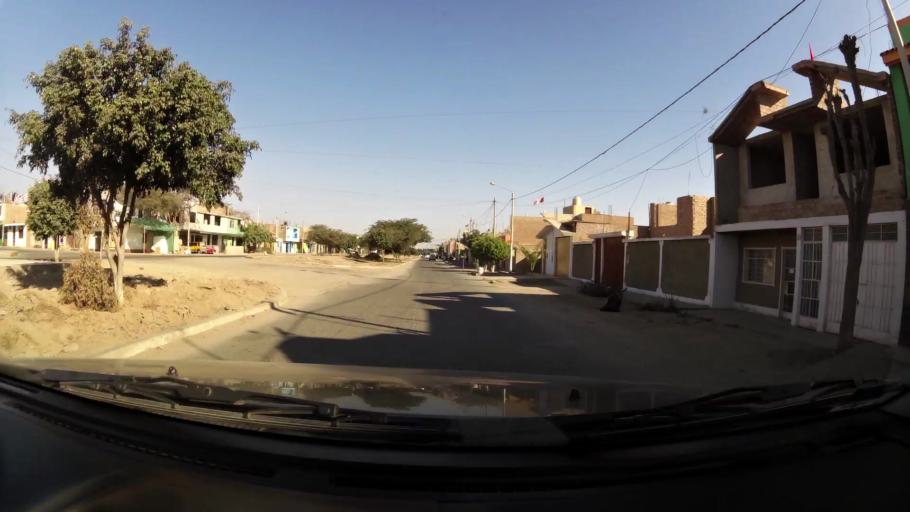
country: PE
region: Ica
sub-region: Provincia de Ica
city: La Tinguina
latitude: -14.0411
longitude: -75.7067
